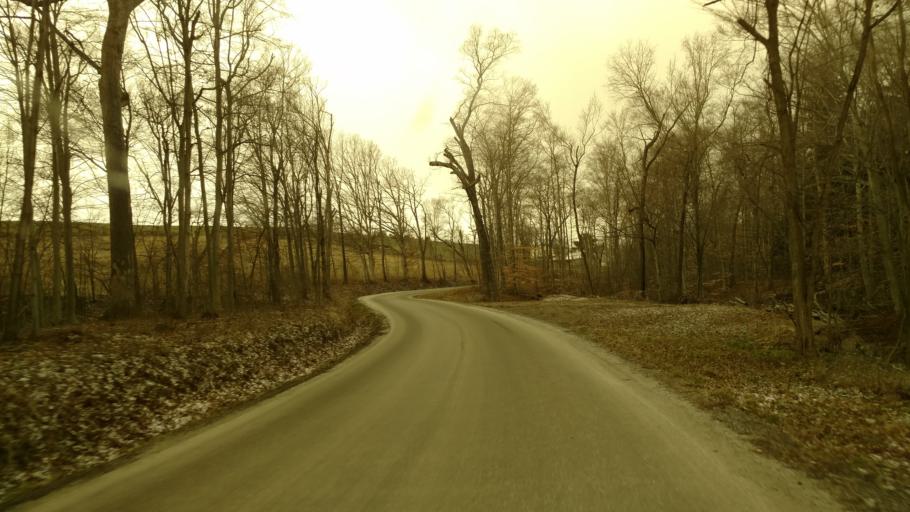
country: US
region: Ohio
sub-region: Tuscarawas County
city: Sugarcreek
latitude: 40.4461
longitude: -81.7754
